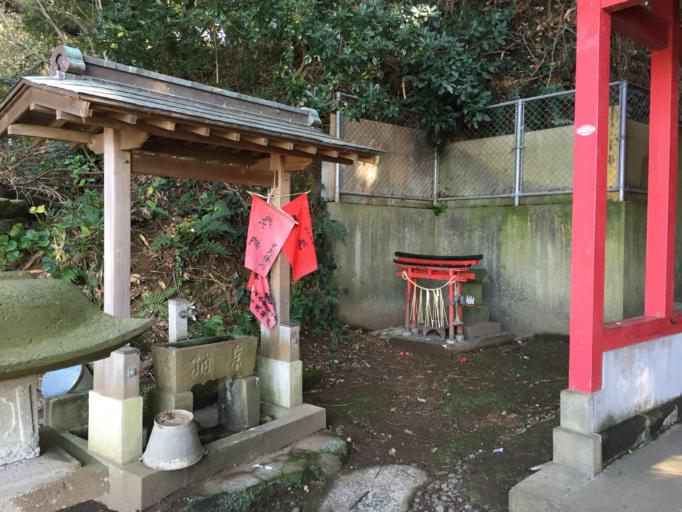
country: JP
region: Kanagawa
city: Miura
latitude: 35.1397
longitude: 139.6251
